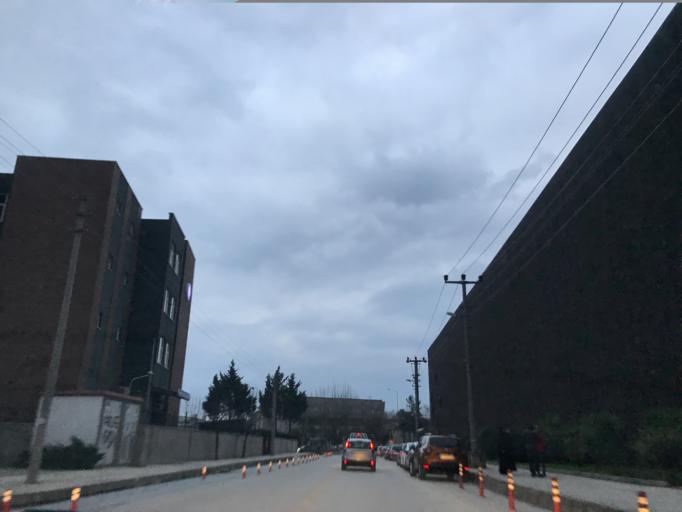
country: TR
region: Yalova
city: Yalova
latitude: 40.6507
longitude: 29.2618
